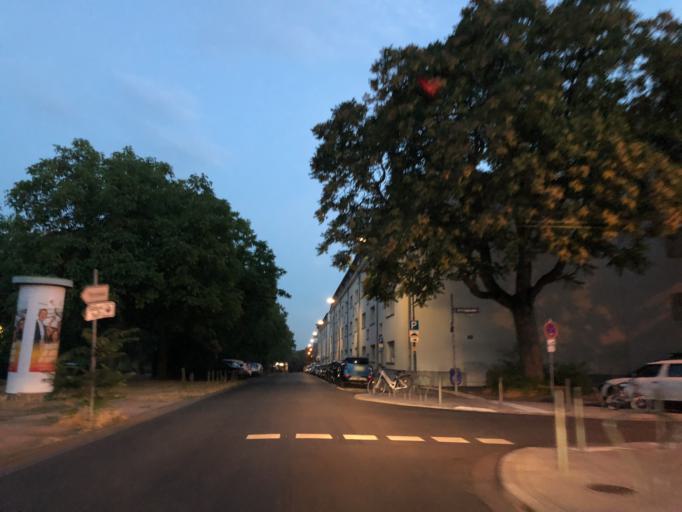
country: DE
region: Hesse
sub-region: Regierungsbezirk Darmstadt
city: Frankfurt am Main
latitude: 50.1270
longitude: 8.7186
